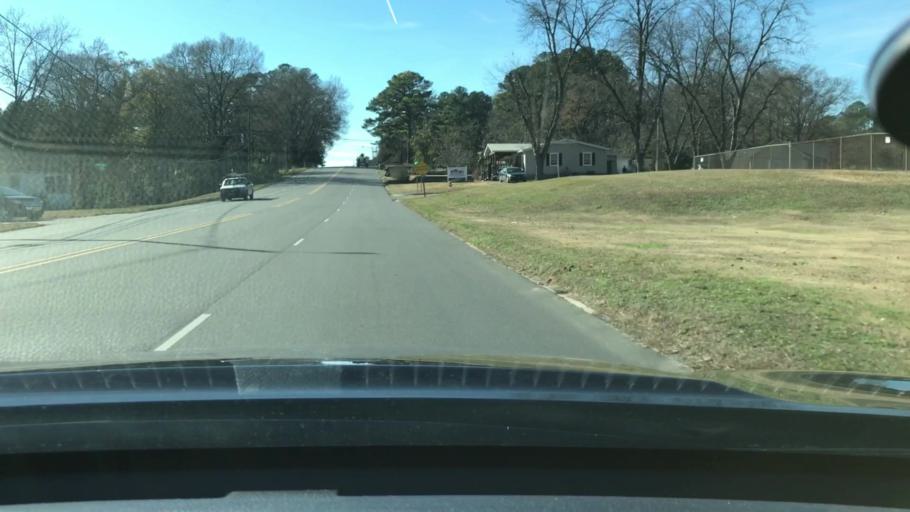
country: US
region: Alabama
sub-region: Talladega County
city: Mignon
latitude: 33.1667
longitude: -86.2693
